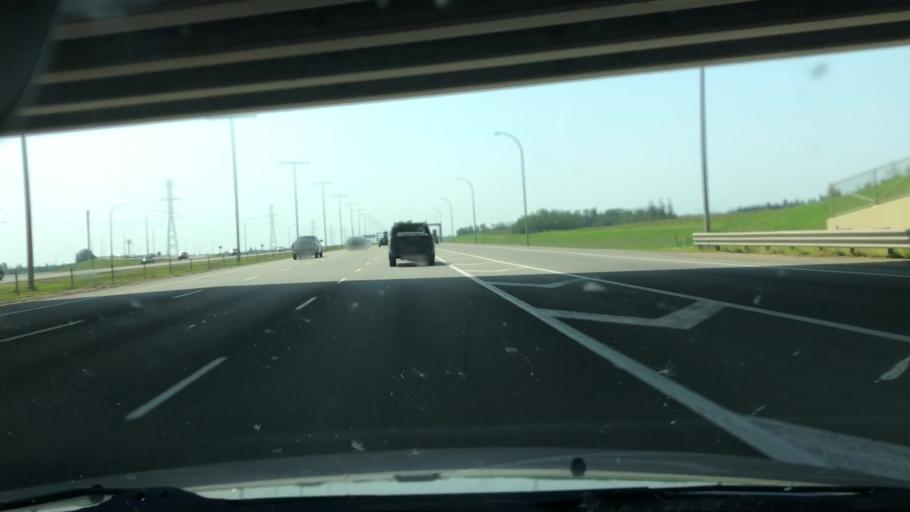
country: CA
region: Alberta
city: St. Albert
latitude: 53.5229
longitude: -113.6596
